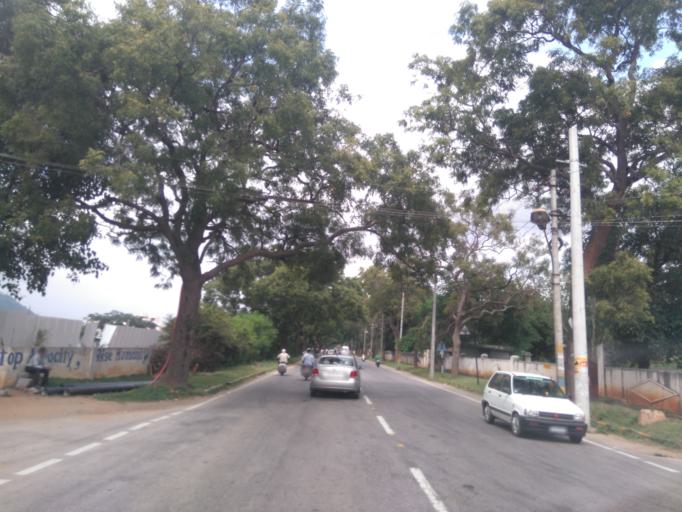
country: IN
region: Karnataka
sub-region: Mysore
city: Mysore
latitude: 12.3011
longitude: 76.6868
